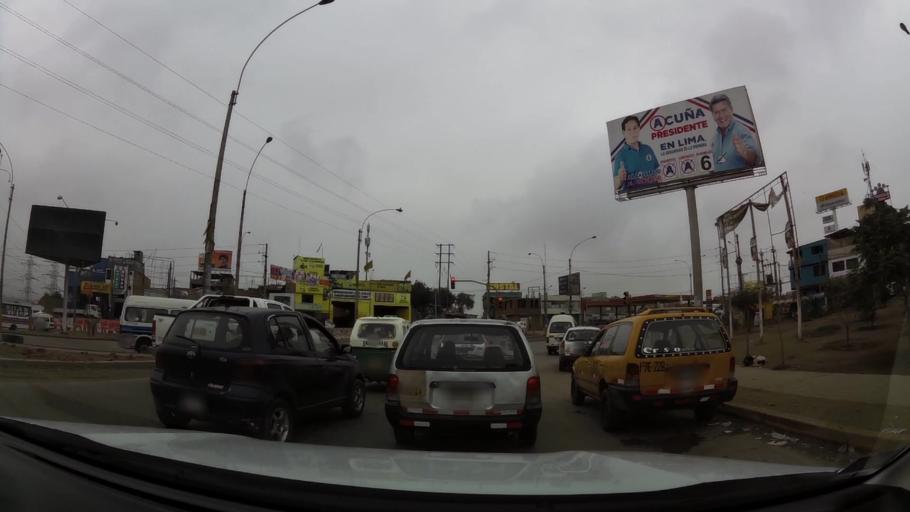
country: PE
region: Lima
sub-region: Lima
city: Surco
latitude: -12.2297
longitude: -76.9101
